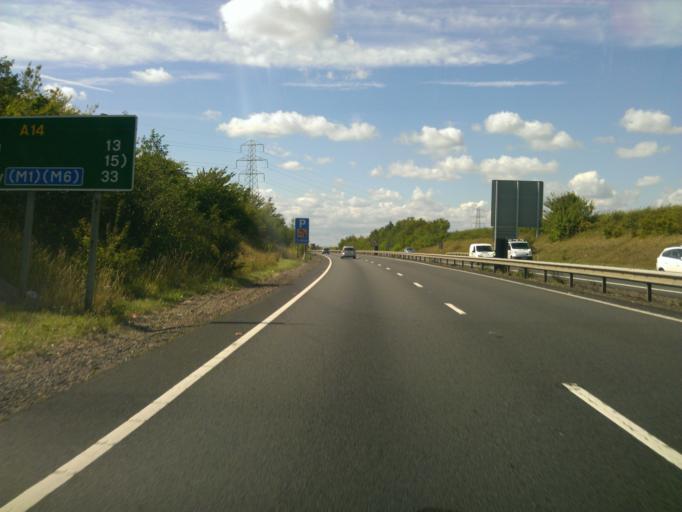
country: GB
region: England
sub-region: Northamptonshire
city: Raunds
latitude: 52.3740
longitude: -0.4631
